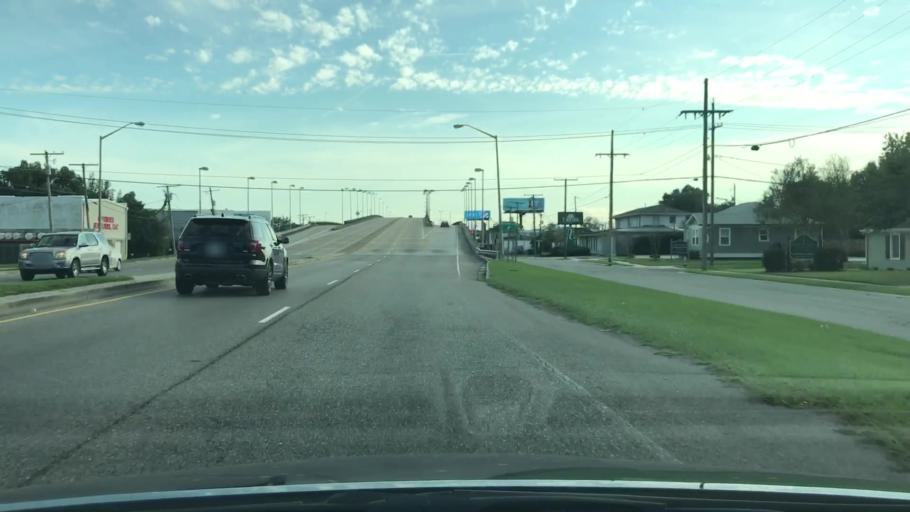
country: US
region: Louisiana
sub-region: Jefferson Parish
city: Metairie
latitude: 29.9786
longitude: -90.1563
